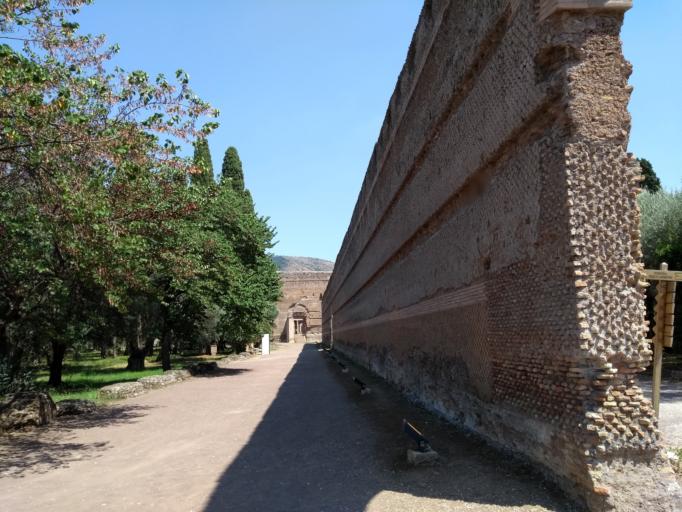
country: IT
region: Latium
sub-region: Citta metropolitana di Roma Capitale
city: Villa Adriana
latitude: 41.9424
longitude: 12.7741
